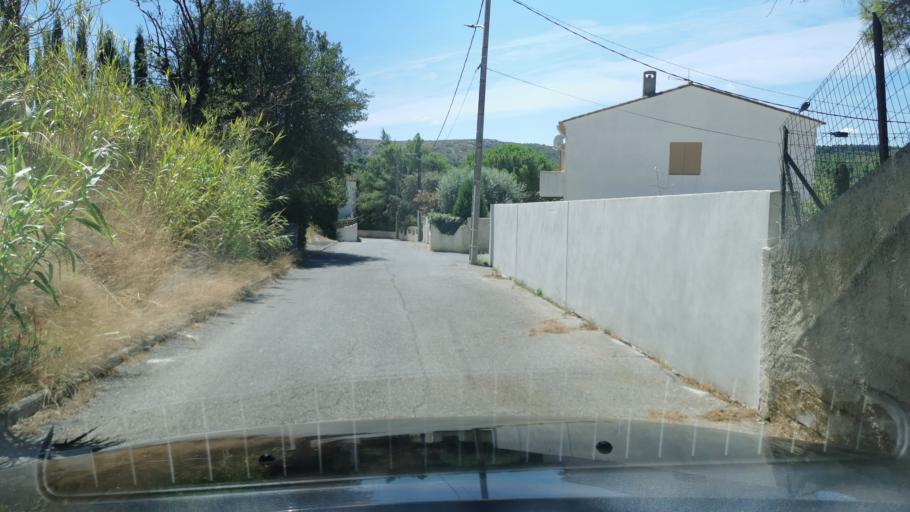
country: FR
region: Languedoc-Roussillon
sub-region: Departement de l'Aude
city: Armissan
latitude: 43.1905
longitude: 3.0940
